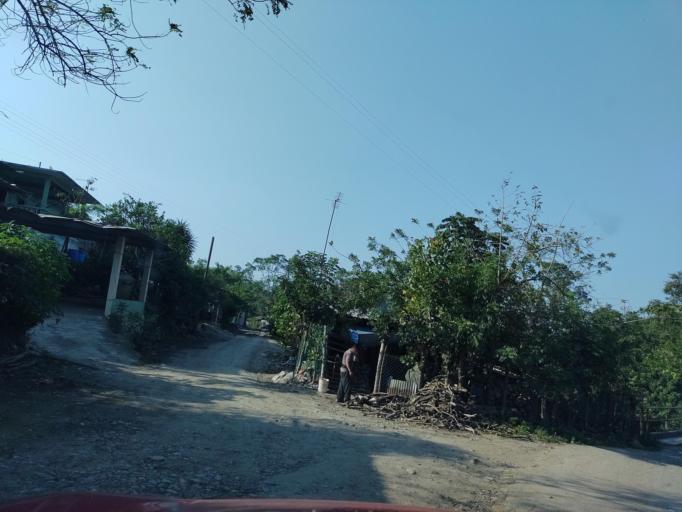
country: MX
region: Veracruz
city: Agua Dulce
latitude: 20.3697
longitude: -97.1841
